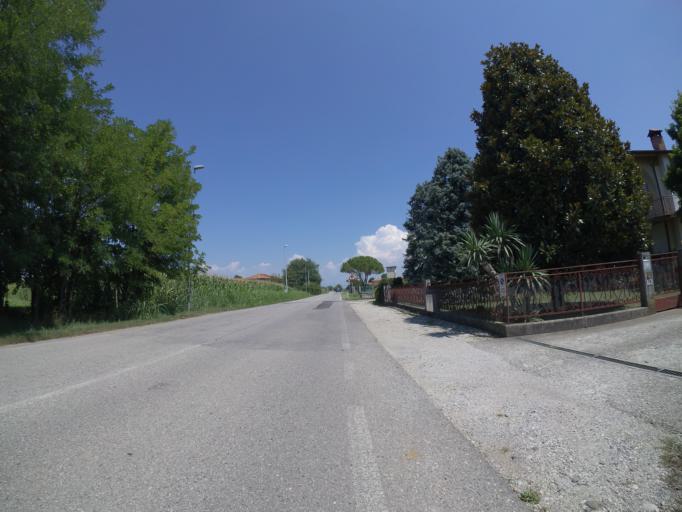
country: IT
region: Friuli Venezia Giulia
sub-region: Provincia di Udine
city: Mortegliano
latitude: 45.9267
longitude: 13.1515
